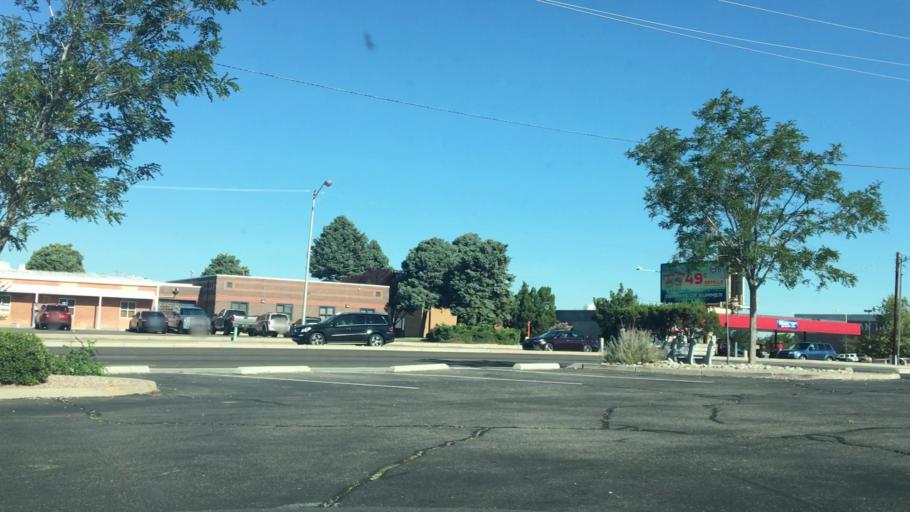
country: US
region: New Mexico
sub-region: Bernalillo County
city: Albuquerque
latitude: 35.1083
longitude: -106.6038
